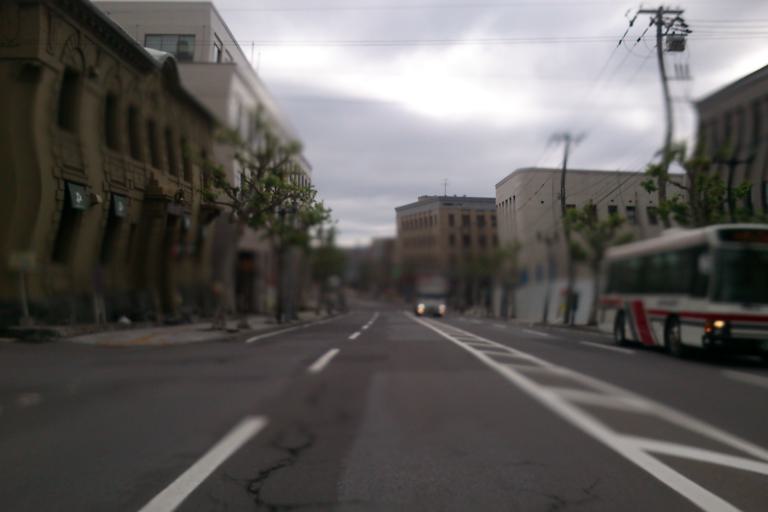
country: JP
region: Hokkaido
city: Otaru
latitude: 43.1962
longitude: 140.9993
